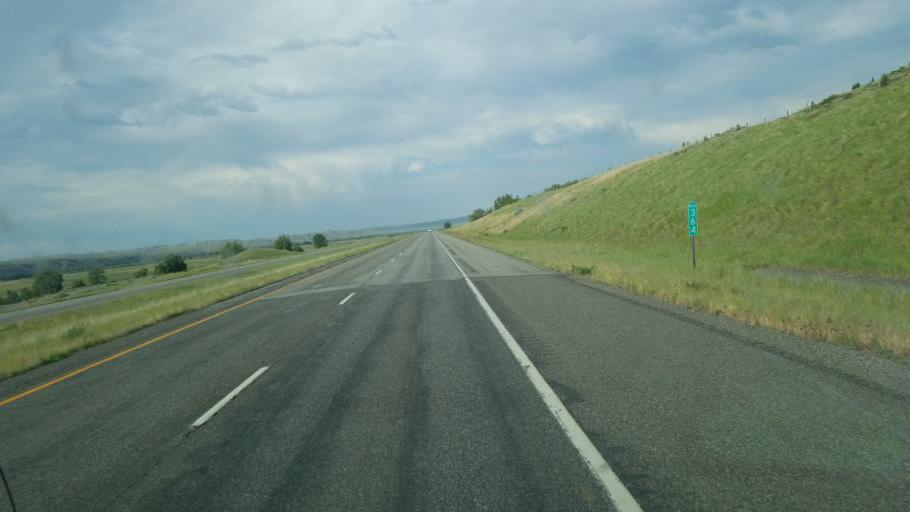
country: US
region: Montana
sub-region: Sweet Grass County
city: Big Timber
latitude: 45.7952
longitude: -110.0352
